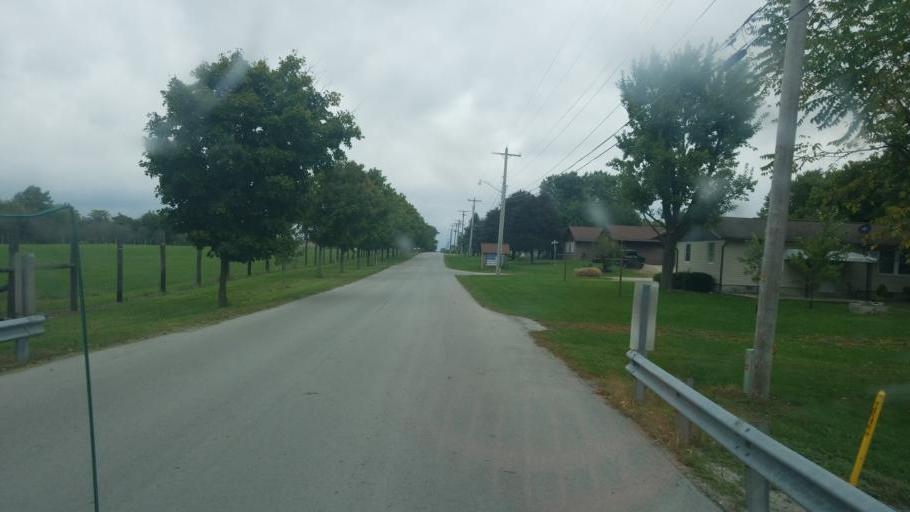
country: US
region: Ohio
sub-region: Seneca County
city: Fostoria
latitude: 41.1134
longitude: -83.5163
